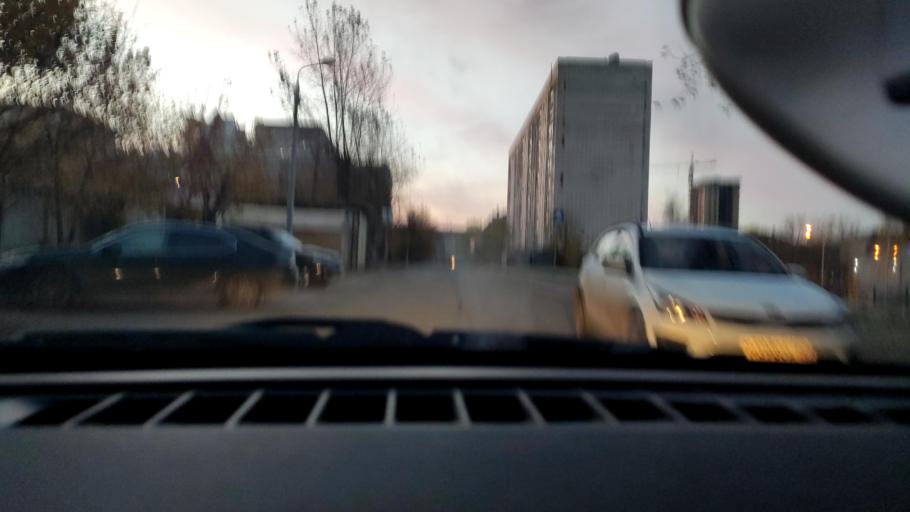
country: RU
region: Perm
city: Kondratovo
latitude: 57.9790
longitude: 56.1790
